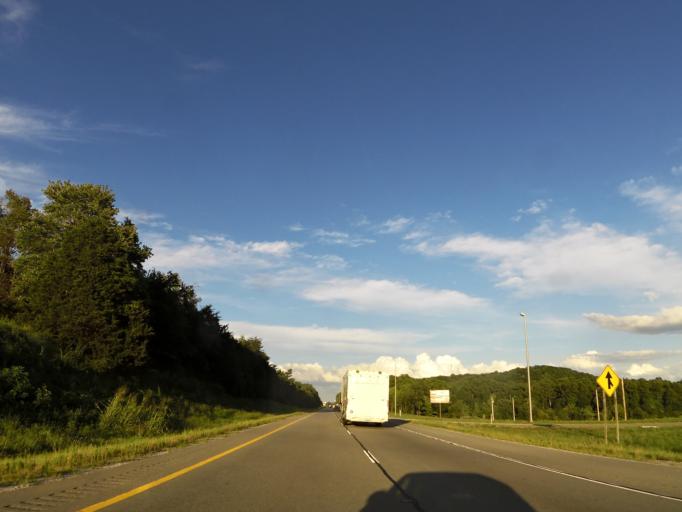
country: US
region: Tennessee
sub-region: Putnam County
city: Cookeville
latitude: 36.1369
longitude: -85.5289
